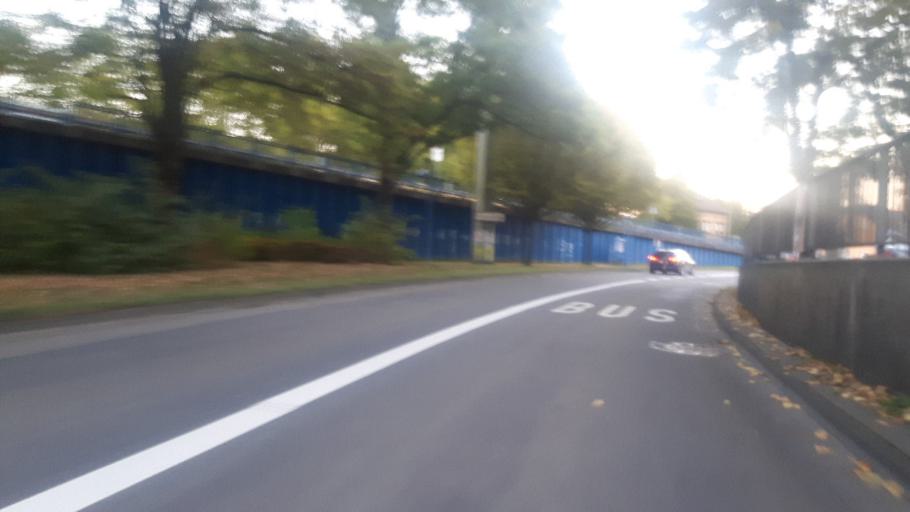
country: DE
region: North Rhine-Westphalia
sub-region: Regierungsbezirk Arnsberg
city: Siegen
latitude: 50.8675
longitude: 8.0086
